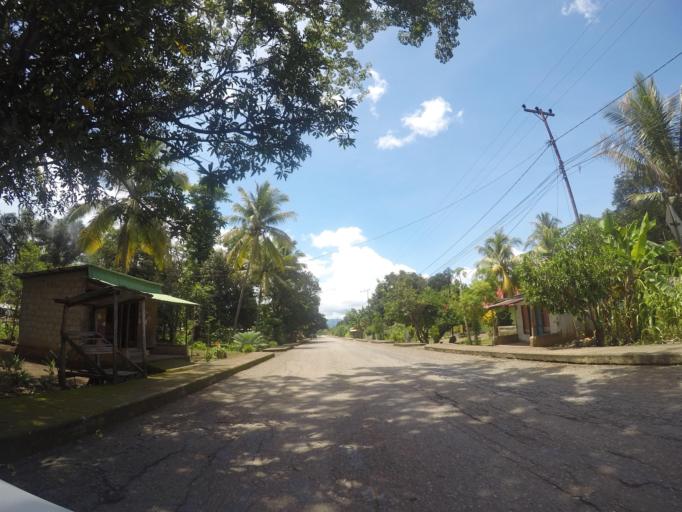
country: TL
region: Bobonaro
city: Maliana
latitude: -8.9908
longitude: 125.1983
